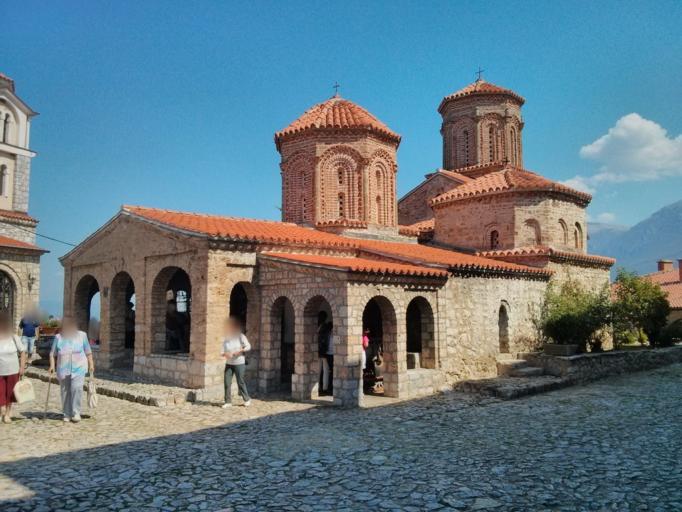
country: AL
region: Korce
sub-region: Rrethi i Pogradecit
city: Bucimas
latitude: 40.9135
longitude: 20.7409
